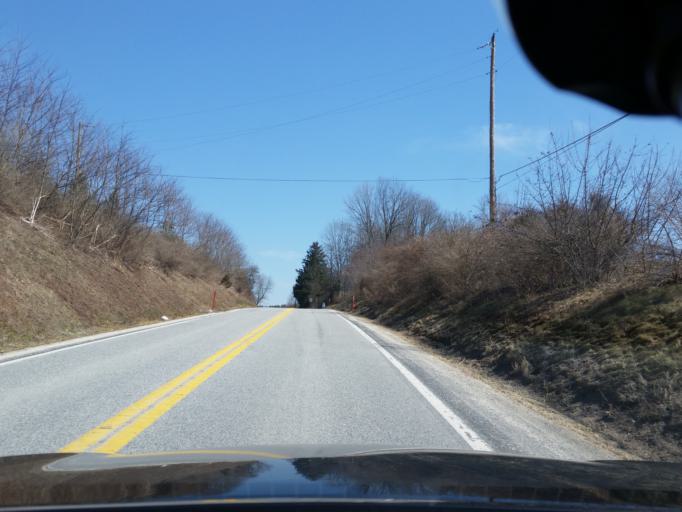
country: US
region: Pennsylvania
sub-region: Cumberland County
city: Schlusser
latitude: 40.3219
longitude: -77.1091
